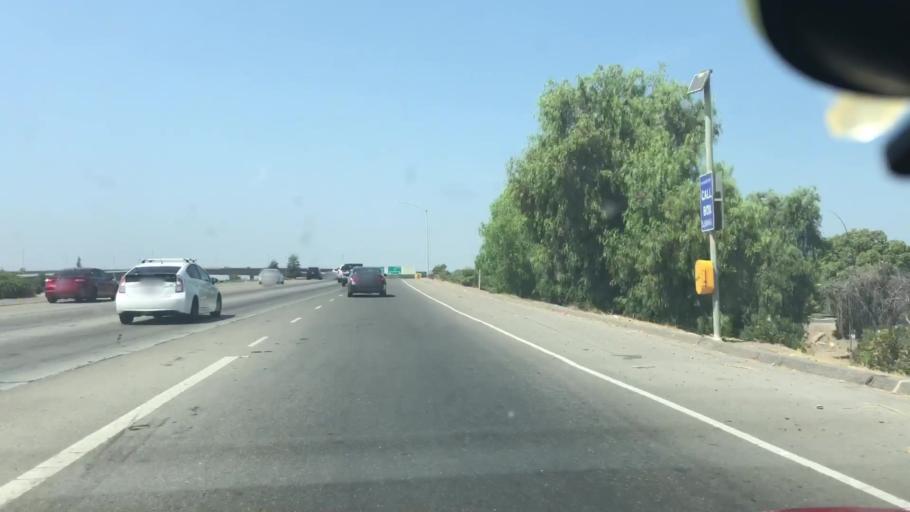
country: US
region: California
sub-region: San Joaquin County
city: Stockton
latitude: 37.9439
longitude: -121.2866
